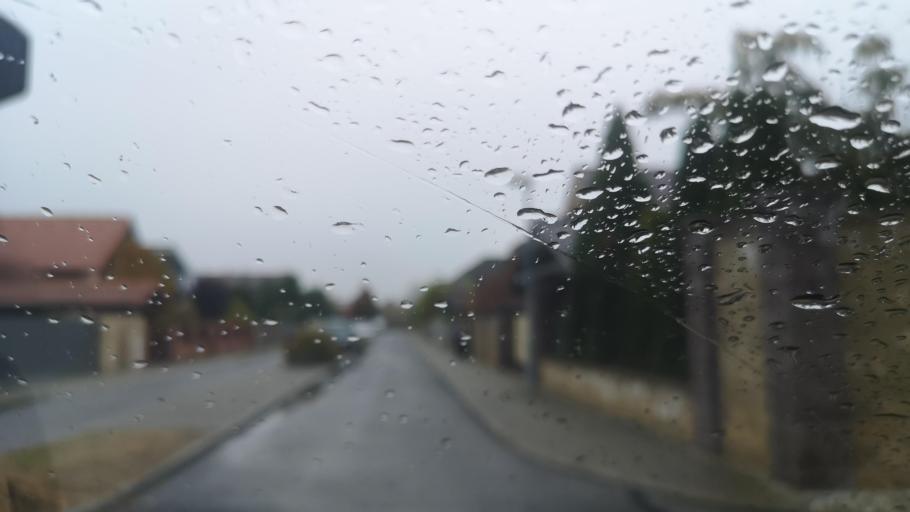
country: SK
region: Nitriansky
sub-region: Okres Nitra
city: Nitra
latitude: 48.3030
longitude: 18.1170
